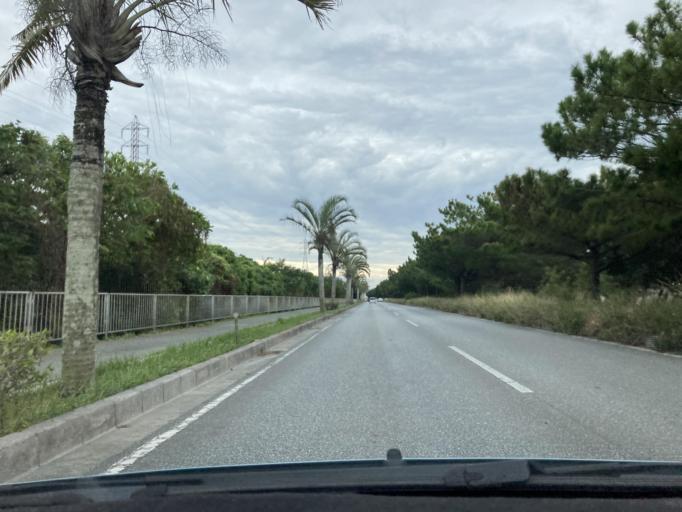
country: JP
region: Okinawa
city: Okinawa
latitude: 26.3908
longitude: 127.7553
